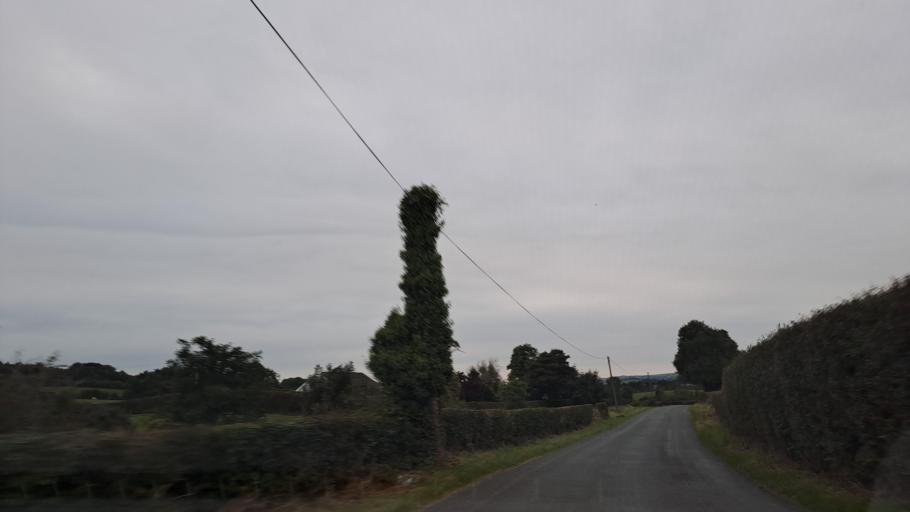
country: IE
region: Ulster
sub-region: County Monaghan
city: Carrickmacross
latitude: 54.0276
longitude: -6.8015
